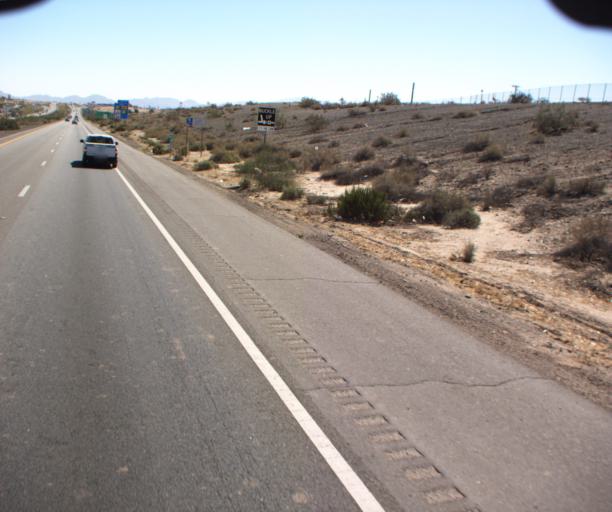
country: US
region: Arizona
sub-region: Yuma County
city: Yuma
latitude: 32.6920
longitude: -114.5985
